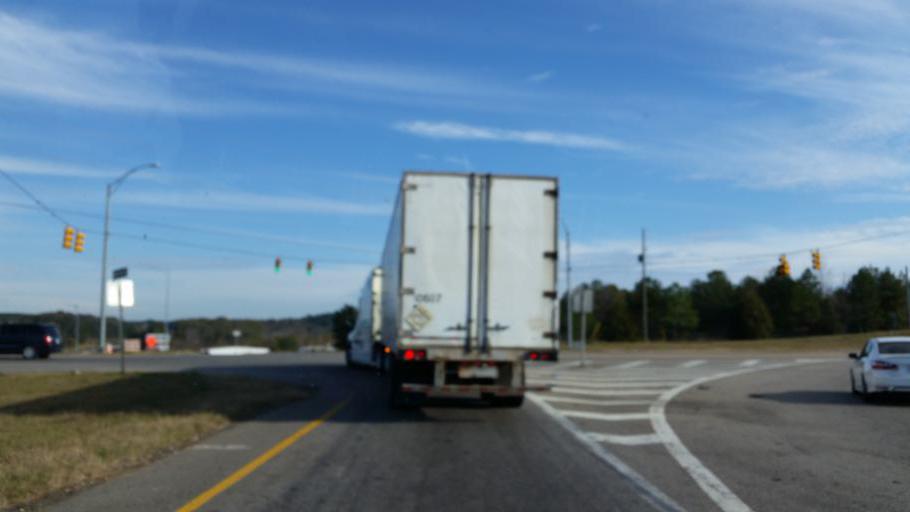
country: US
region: Alabama
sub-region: Tuscaloosa County
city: Holt
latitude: 33.1720
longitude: -87.4480
